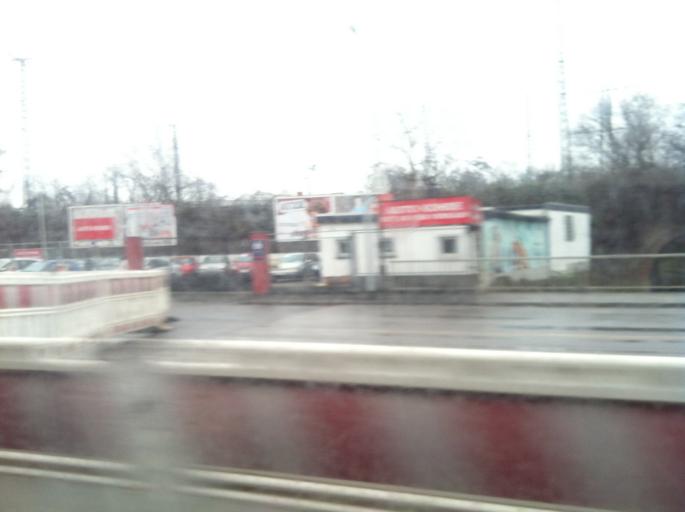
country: DE
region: Hesse
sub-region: Regierungsbezirk Darmstadt
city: Wiesbaden
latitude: 50.0363
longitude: 8.2592
